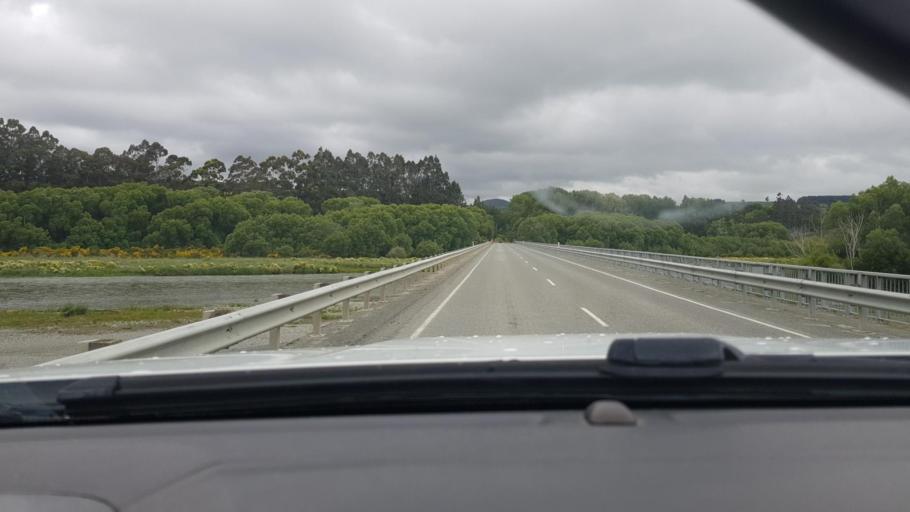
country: NZ
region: Southland
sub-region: Southland District
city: Winton
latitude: -45.8951
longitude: 168.3606
